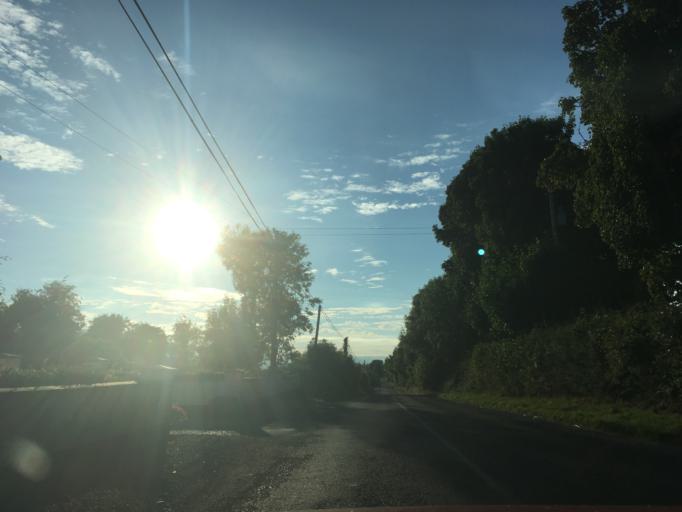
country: IE
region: Munster
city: Cashel
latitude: 52.4426
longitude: -7.8878
